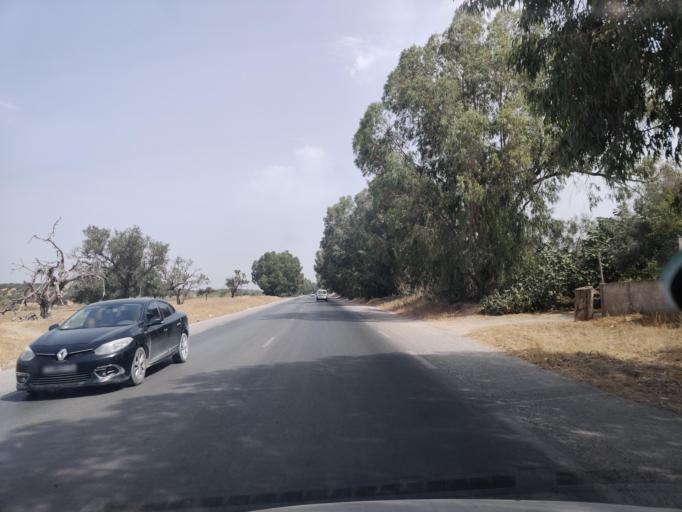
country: TN
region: Nabul
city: Al Hammamat
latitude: 36.4478
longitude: 10.5724
